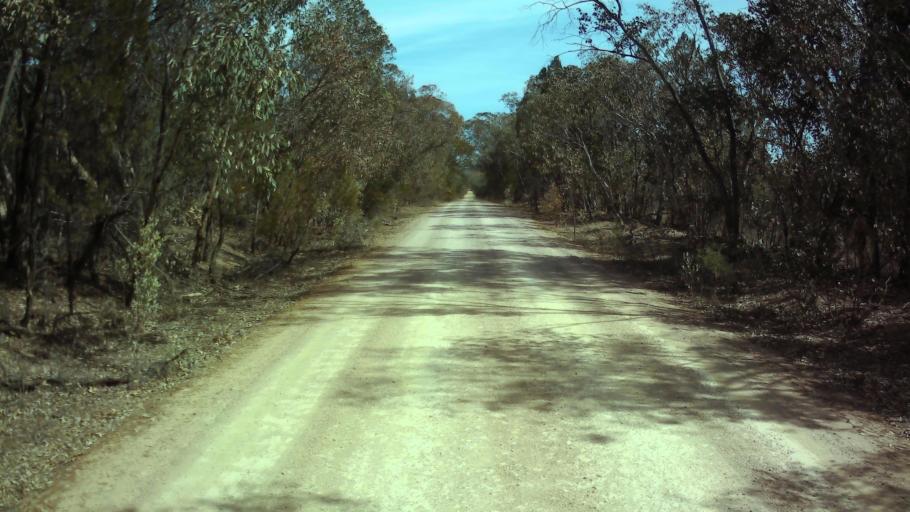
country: AU
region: New South Wales
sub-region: Weddin
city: Grenfell
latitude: -33.8803
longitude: 148.1507
